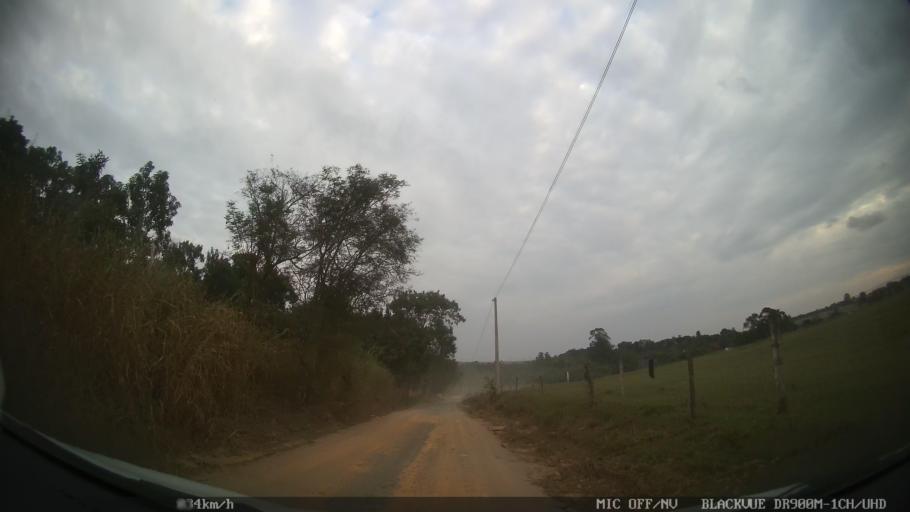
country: BR
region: Sao Paulo
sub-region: Santa Barbara D'Oeste
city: Santa Barbara d'Oeste
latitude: -22.6924
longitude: -47.3874
